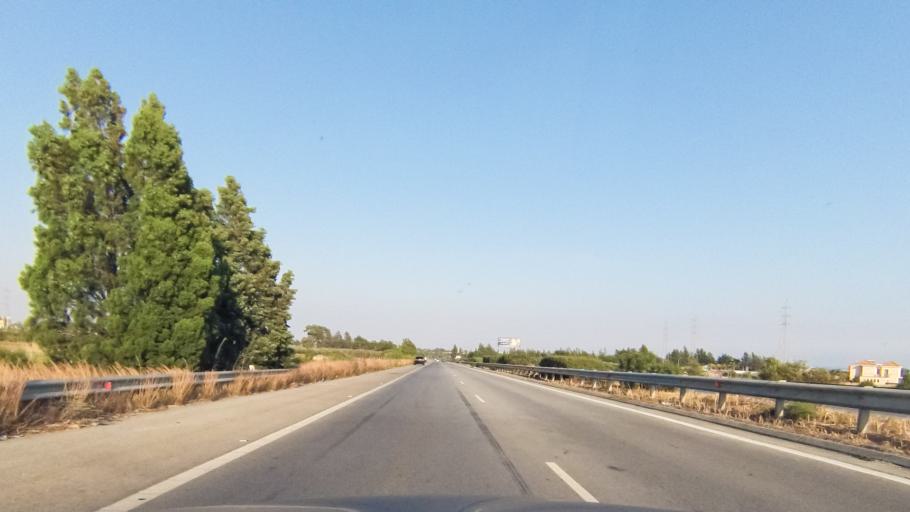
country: CY
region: Limassol
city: Ypsonas
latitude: 34.6911
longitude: 32.9784
